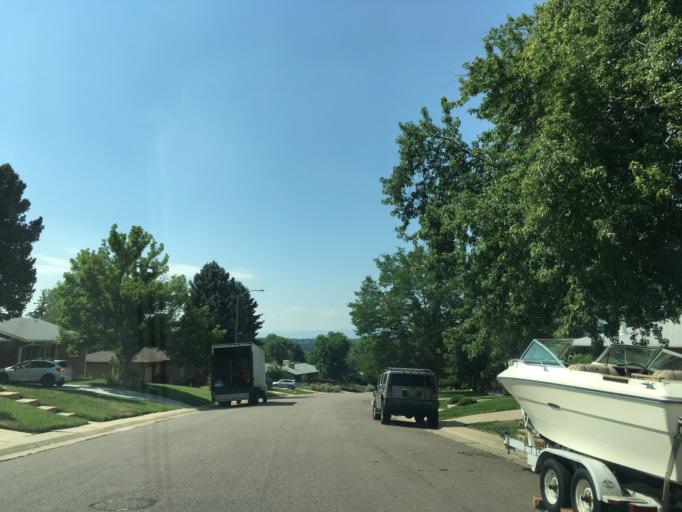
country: US
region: Colorado
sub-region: Arapahoe County
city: Sheridan
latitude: 39.6666
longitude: -105.0449
